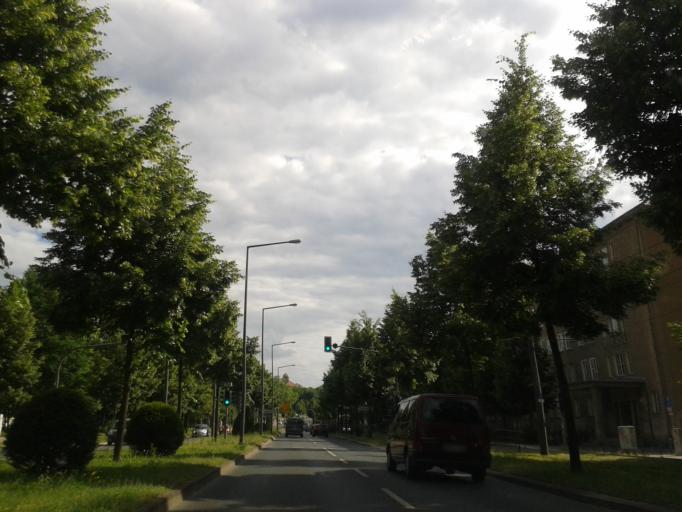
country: DE
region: Saxony
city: Dresden
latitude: 51.0363
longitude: 13.7320
